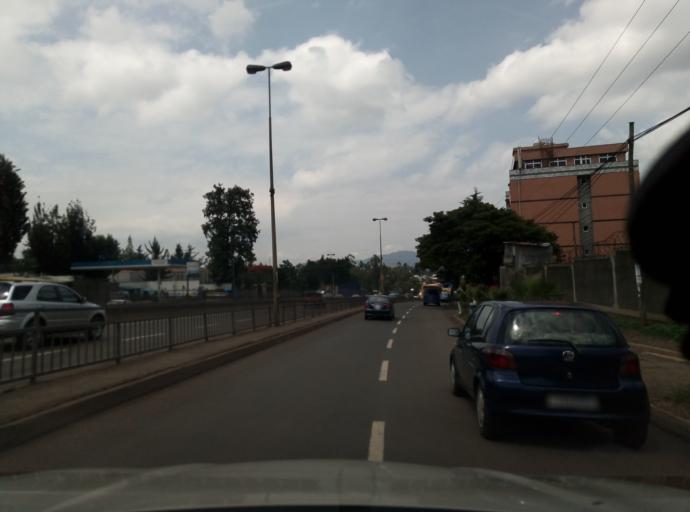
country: ET
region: Adis Abeba
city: Addis Ababa
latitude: 8.9956
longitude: 38.7182
